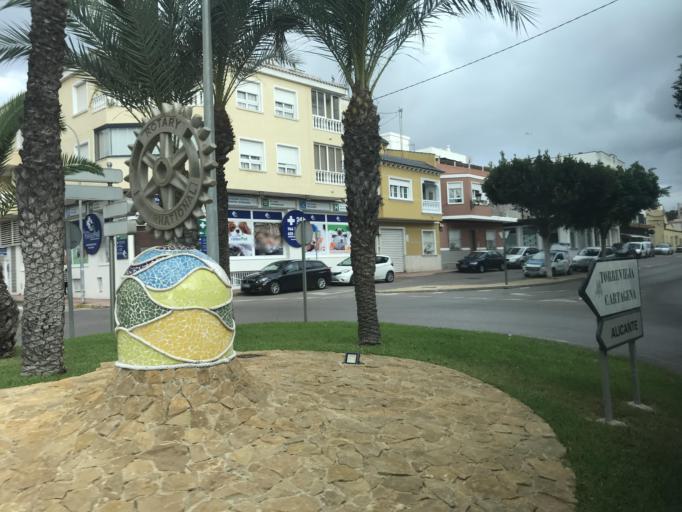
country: ES
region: Valencia
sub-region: Provincia de Alicante
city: Guardamar del Segura
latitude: 38.0828
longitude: -0.6548
